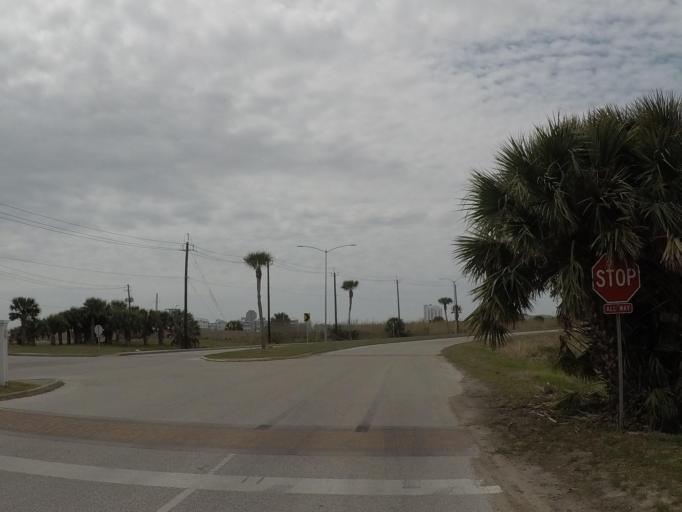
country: US
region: Texas
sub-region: Galveston County
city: Galveston
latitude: 29.3152
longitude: -94.7584
